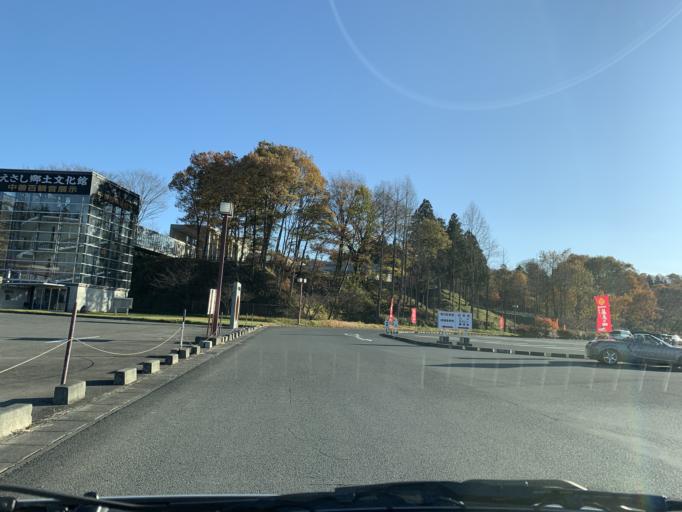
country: JP
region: Iwate
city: Mizusawa
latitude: 39.1975
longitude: 141.1905
